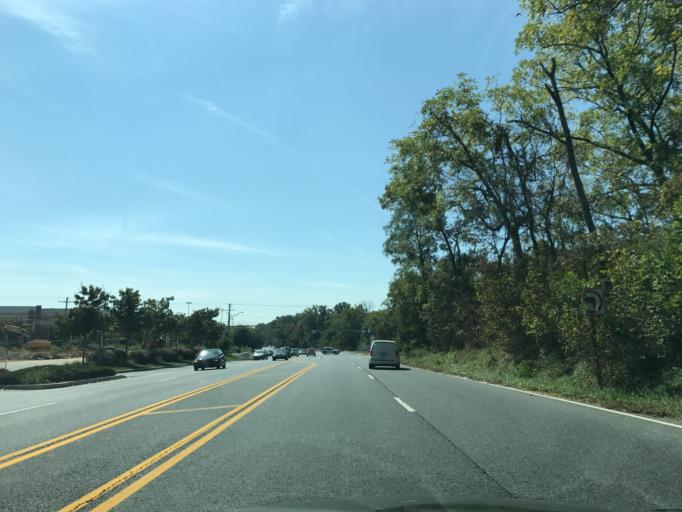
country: US
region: Maryland
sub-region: Anne Arundel County
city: Jessup
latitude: 39.1900
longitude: -76.7963
